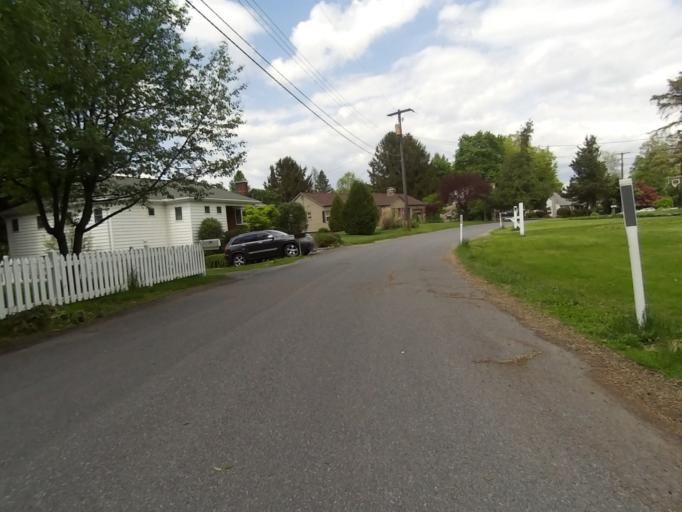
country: US
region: Pennsylvania
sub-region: Centre County
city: Houserville
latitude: 40.8124
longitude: -77.8403
